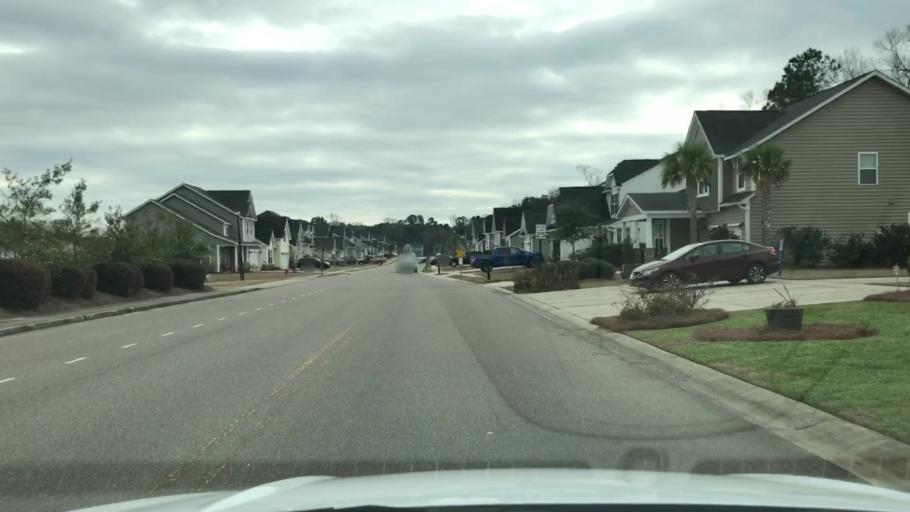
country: US
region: South Carolina
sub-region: Berkeley County
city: Goose Creek
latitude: 33.0319
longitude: -80.0225
